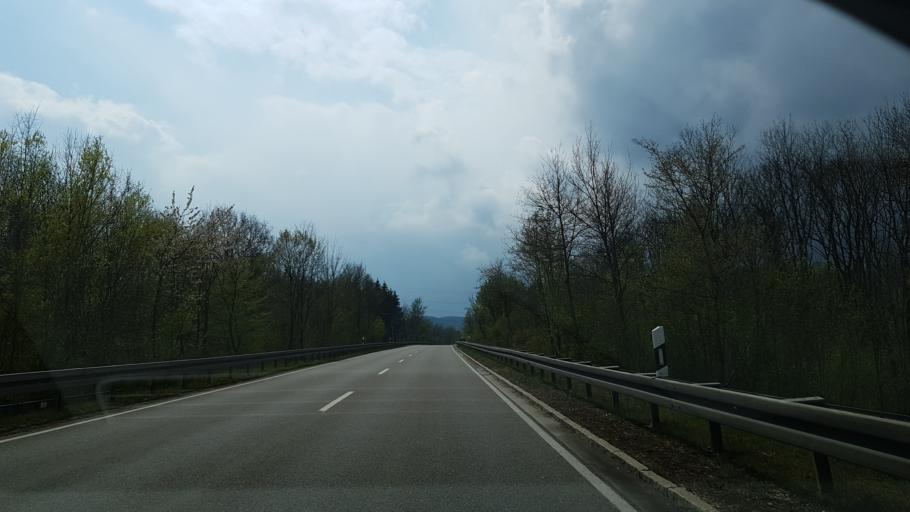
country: DE
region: Baden-Wuerttemberg
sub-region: Tuebingen Region
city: Dietenheim
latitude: 48.2044
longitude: 10.0864
